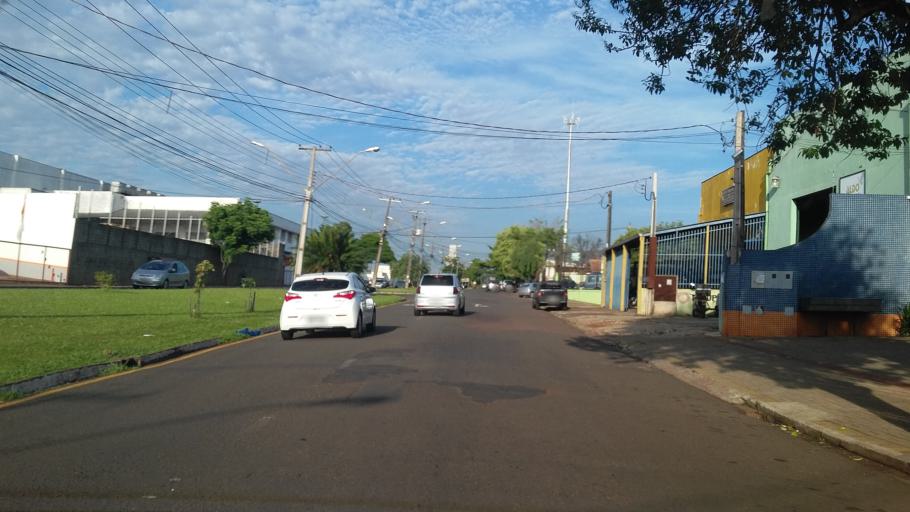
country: BR
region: Parana
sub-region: Londrina
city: Londrina
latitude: -23.2967
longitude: -51.1950
